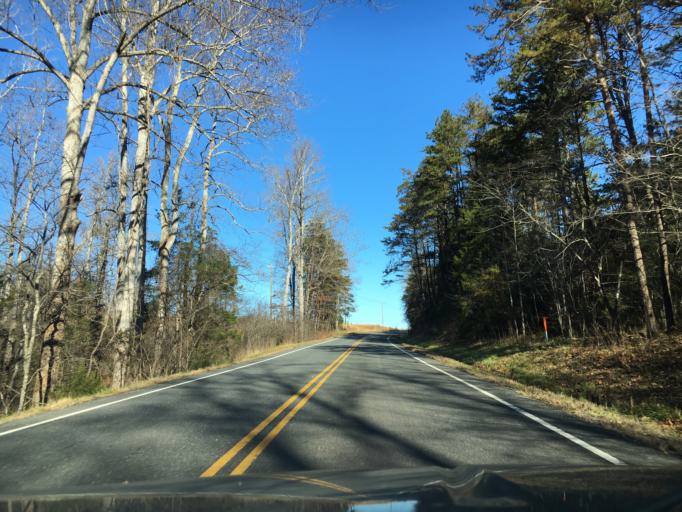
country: US
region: Virginia
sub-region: Buckingham County
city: Buckingham
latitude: 37.5126
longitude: -78.6181
